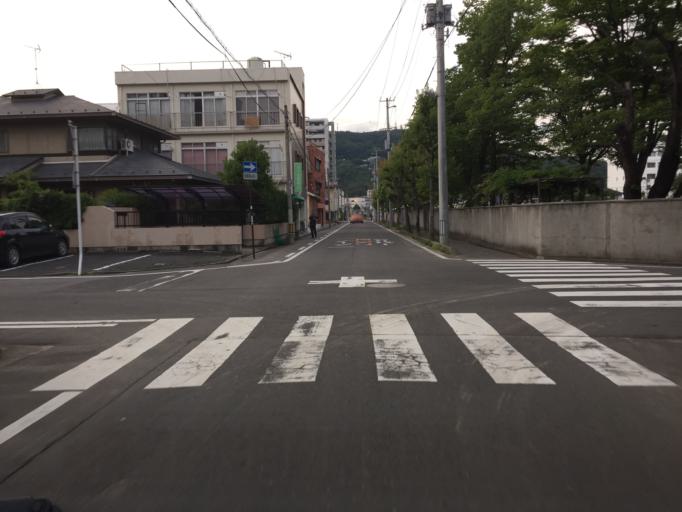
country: JP
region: Fukushima
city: Fukushima-shi
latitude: 37.7624
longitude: 140.4719
